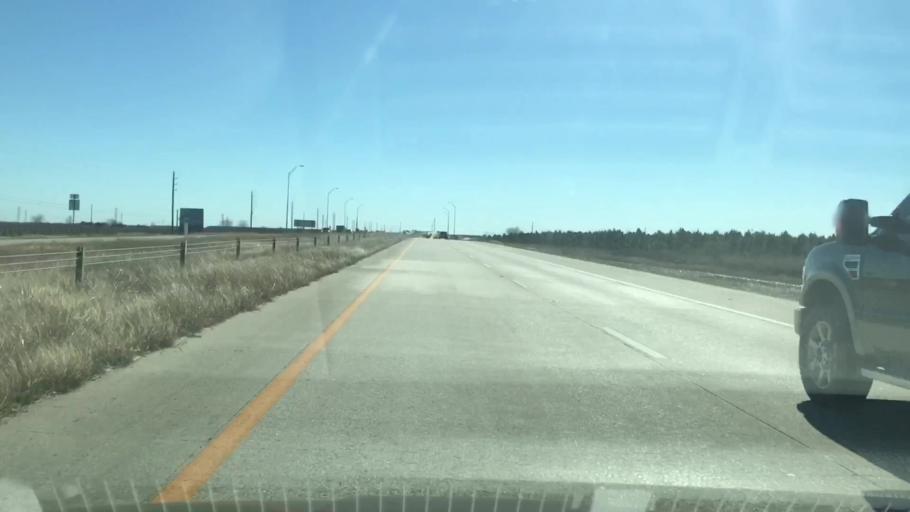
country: US
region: Texas
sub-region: Harris County
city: Cypress
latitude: 29.9312
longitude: -95.7633
